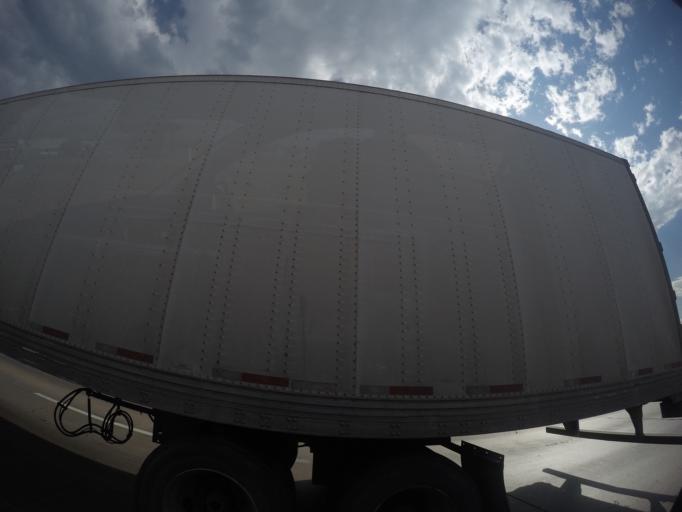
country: MX
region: Queretaro
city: El Sauz
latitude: 20.4668
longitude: -100.1032
